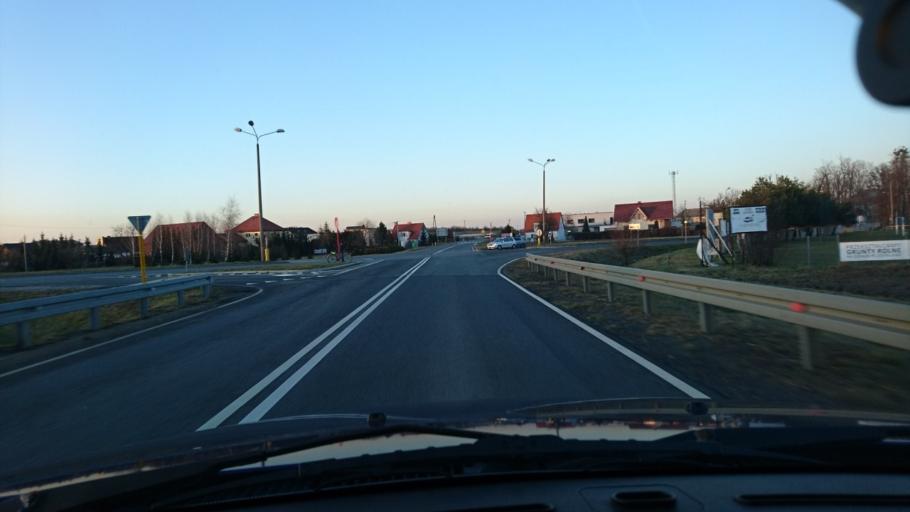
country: PL
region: Silesian Voivodeship
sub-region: Powiat gliwicki
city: Wielowies
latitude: 50.5032
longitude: 18.6048
